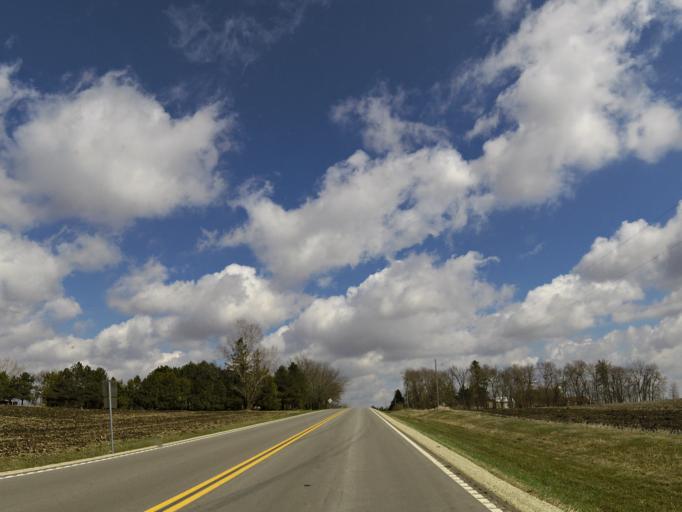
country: US
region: Minnesota
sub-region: Dodge County
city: Dodge Center
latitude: 44.0881
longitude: -92.8982
